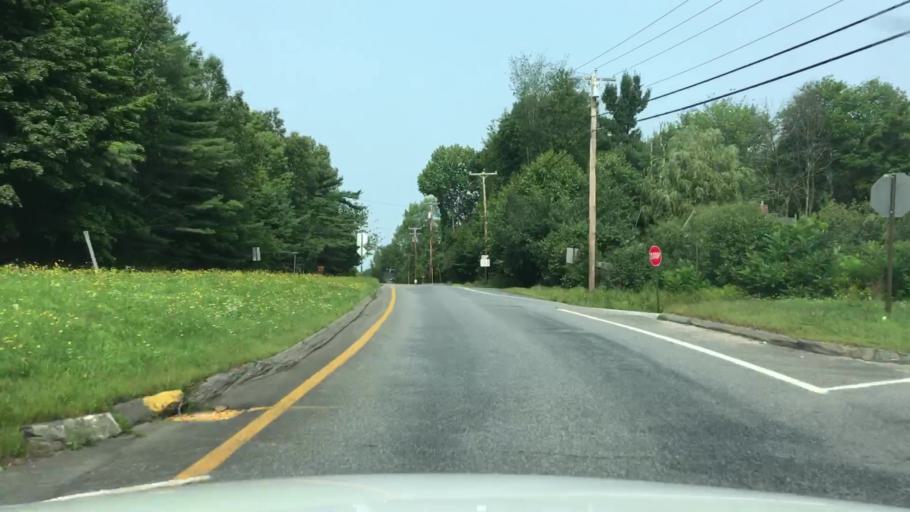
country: US
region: Maine
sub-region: Kennebec County
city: Winthrop
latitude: 44.3214
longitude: -69.9795
